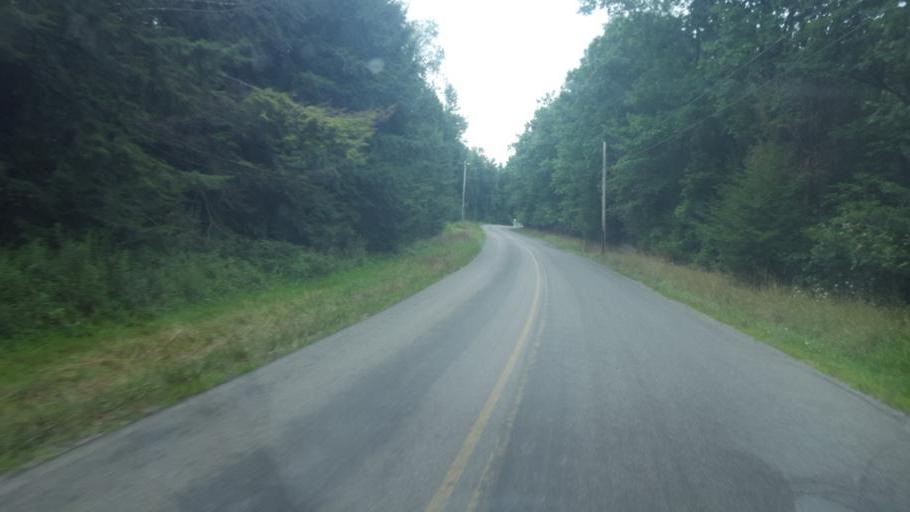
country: US
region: Pennsylvania
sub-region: Clarion County
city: Marianne
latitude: 41.2008
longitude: -79.4480
